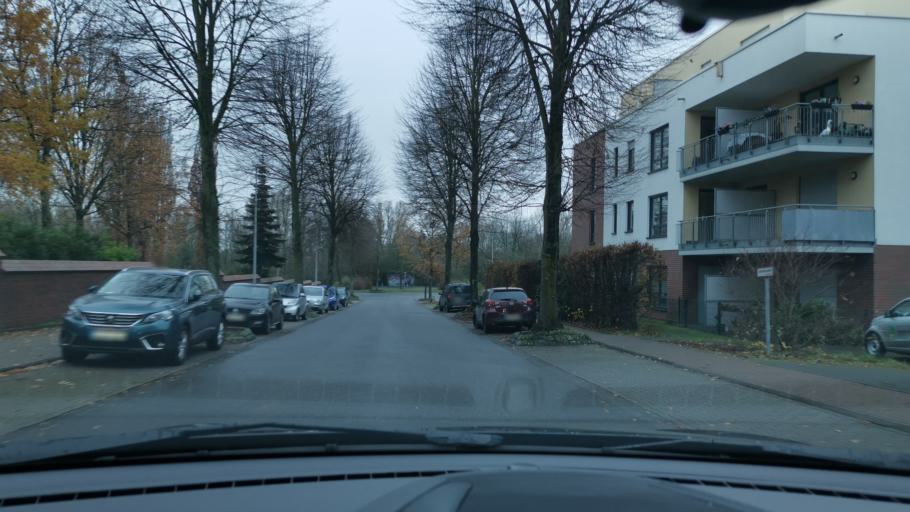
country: DE
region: North Rhine-Westphalia
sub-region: Regierungsbezirk Dusseldorf
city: Juchen
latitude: 51.1076
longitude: 6.5051
